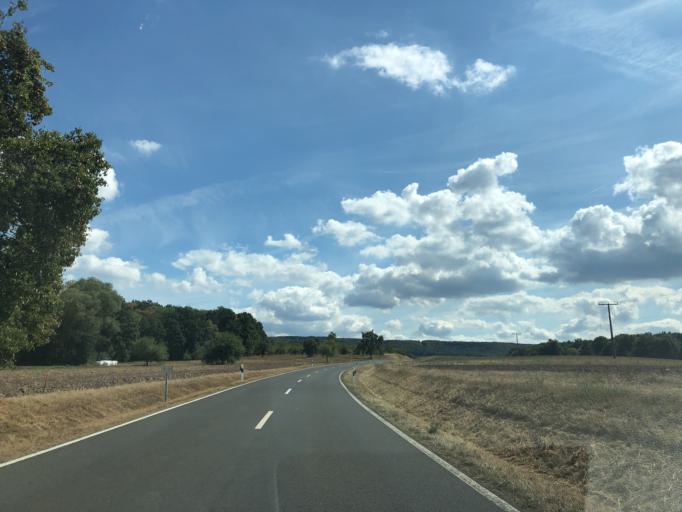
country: DE
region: Bavaria
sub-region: Regierungsbezirk Unterfranken
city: Oberschwarzach
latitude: 49.8448
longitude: 10.4294
